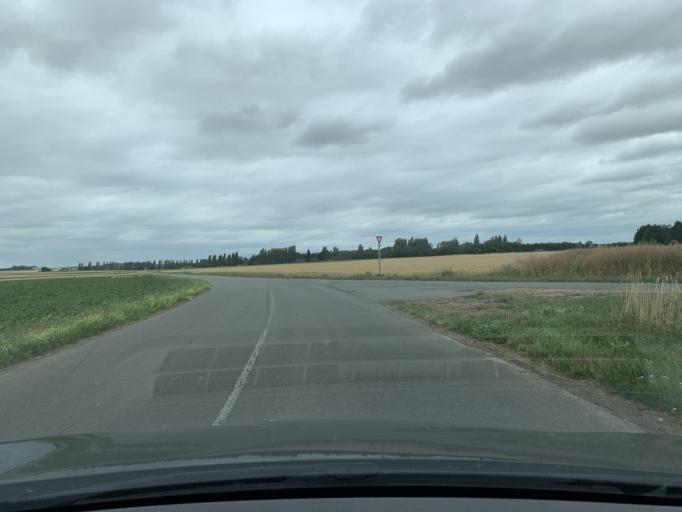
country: FR
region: Nord-Pas-de-Calais
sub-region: Departement du Nord
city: Raillencourt-Sainte-Olle
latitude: 50.2062
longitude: 3.1446
